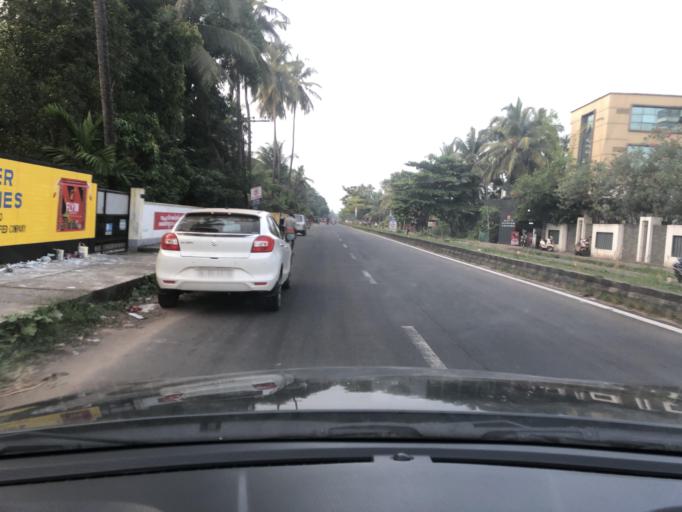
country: IN
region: Kerala
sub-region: Kozhikode
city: Kozhikode
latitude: 11.2918
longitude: 75.7583
